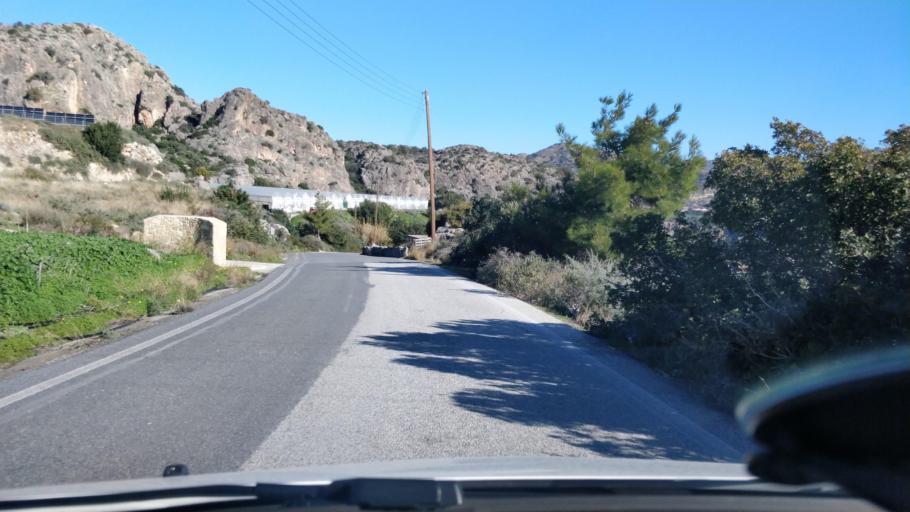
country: GR
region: Crete
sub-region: Nomos Lasithiou
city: Gra Liyia
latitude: 35.0373
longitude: 25.6683
